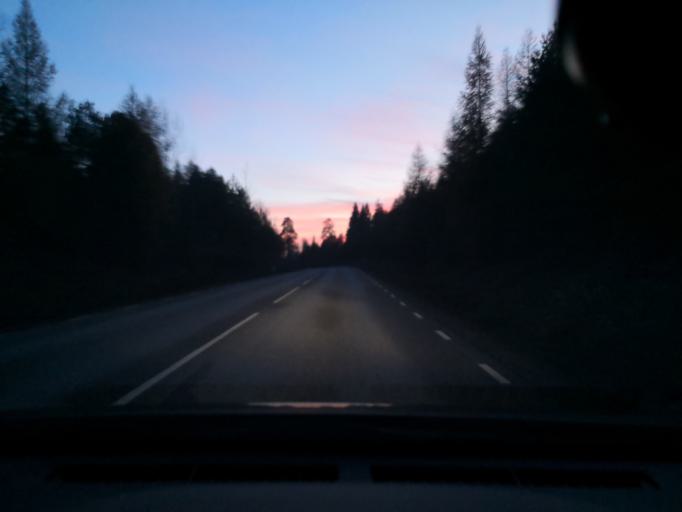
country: SE
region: OErebro
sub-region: Lindesbergs Kommun
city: Frovi
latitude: 59.3818
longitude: 15.4412
